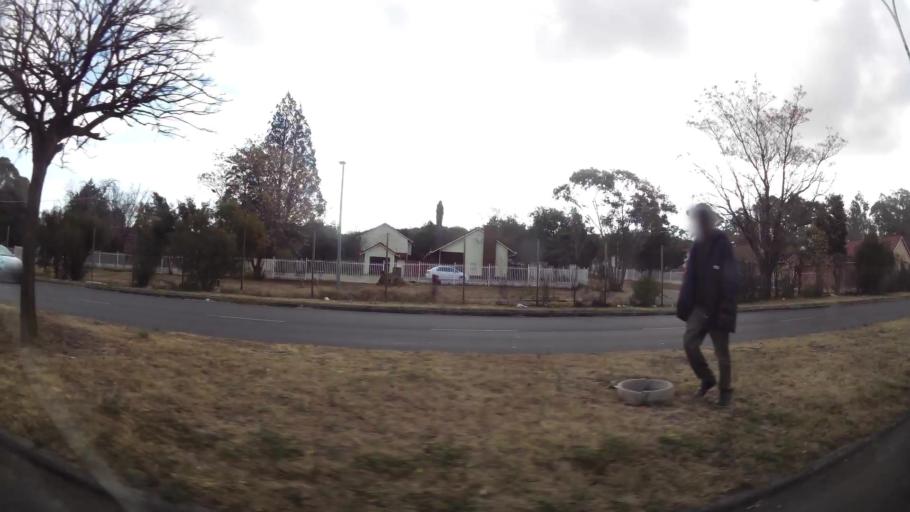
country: ZA
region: Orange Free State
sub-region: Mangaung Metropolitan Municipality
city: Bloemfontein
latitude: -29.0942
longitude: 26.2034
